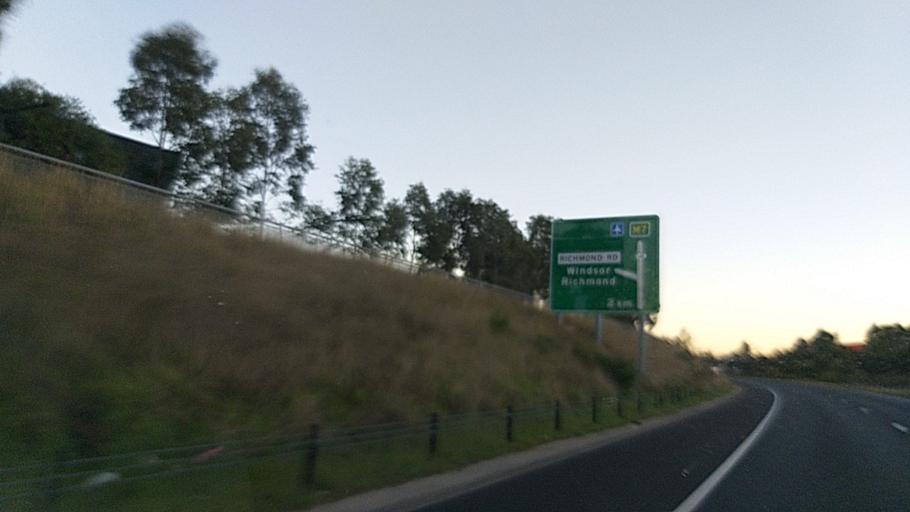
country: AU
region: New South Wales
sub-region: Blacktown
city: Glendenning
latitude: -33.7562
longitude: 150.8475
